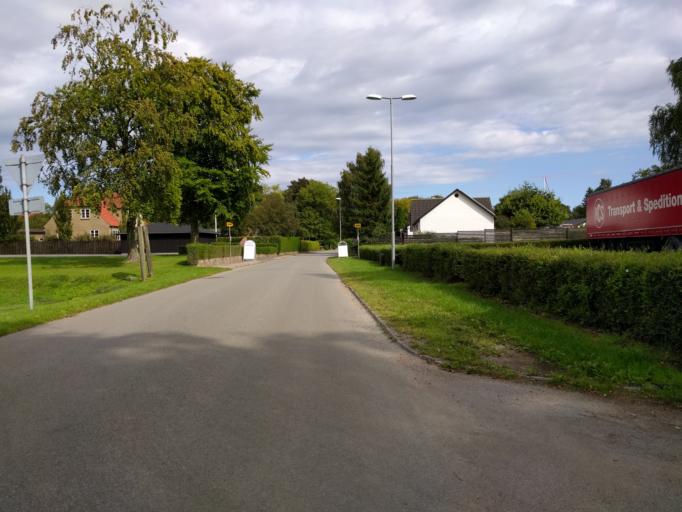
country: DK
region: South Denmark
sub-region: Kerteminde Kommune
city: Munkebo
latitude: 55.4672
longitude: 10.6016
